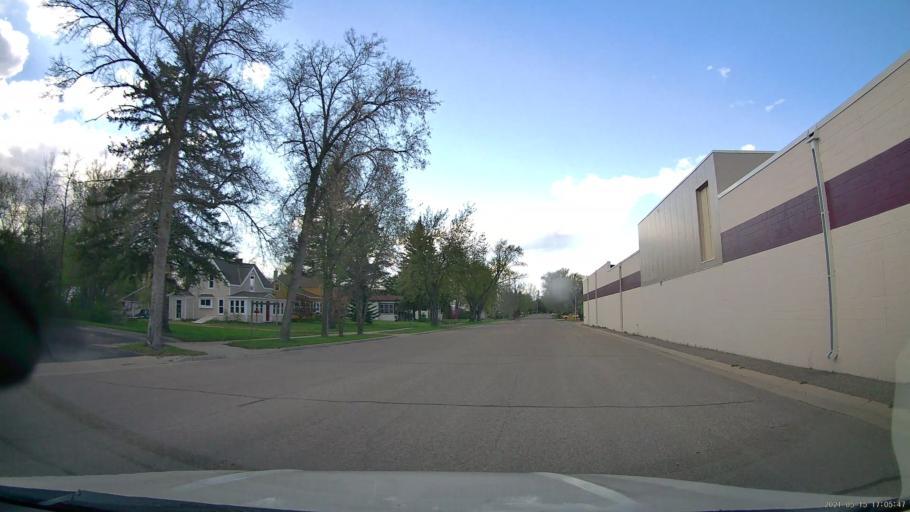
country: US
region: Minnesota
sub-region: Hubbard County
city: Park Rapids
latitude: 46.9223
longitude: -95.0621
